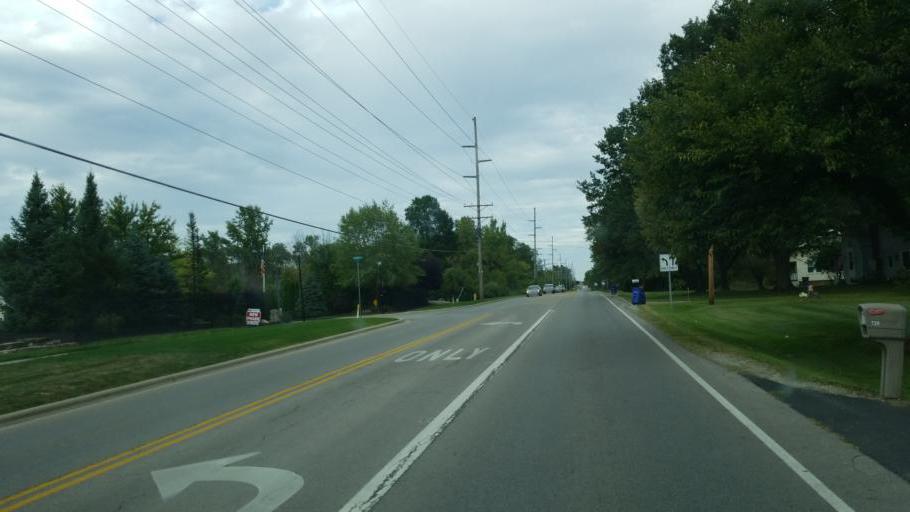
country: US
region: Ohio
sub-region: Franklin County
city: Reynoldsburg
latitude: 39.9647
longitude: -82.8375
